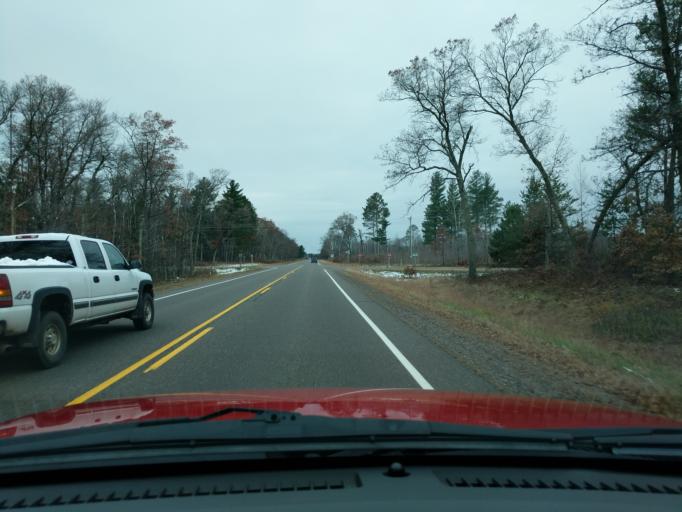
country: US
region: Wisconsin
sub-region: Washburn County
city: Shell Lake
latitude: 45.8145
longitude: -92.1327
